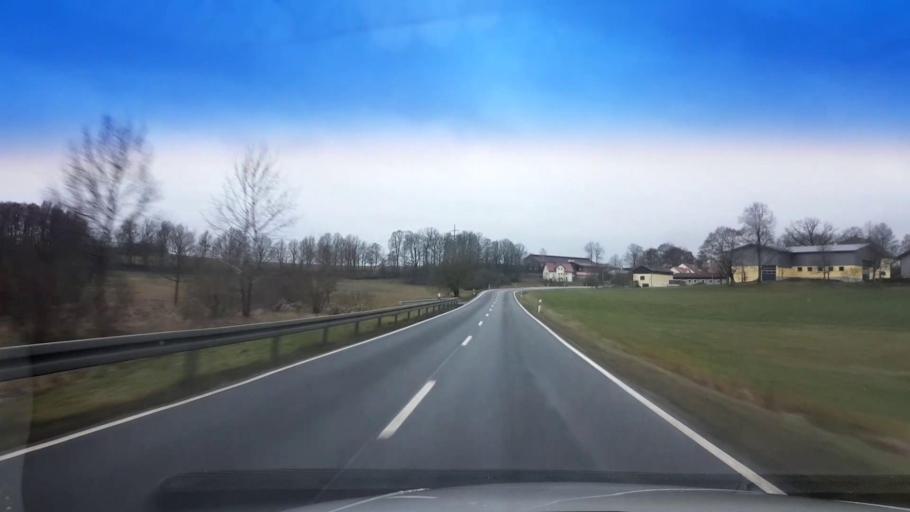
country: DE
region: Bavaria
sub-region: Upper Palatinate
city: Tirschenreuth
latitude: 49.8744
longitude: 12.2988
